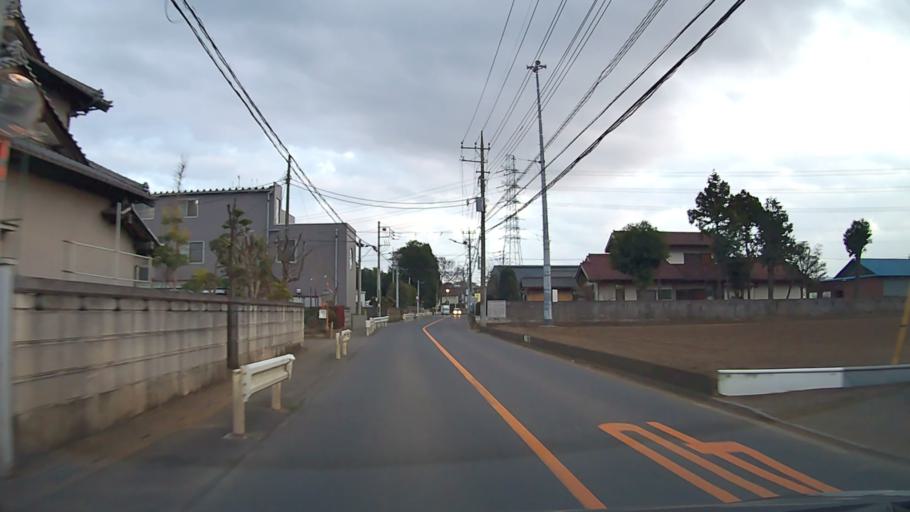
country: JP
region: Saitama
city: Oi
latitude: 35.8252
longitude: 139.5234
